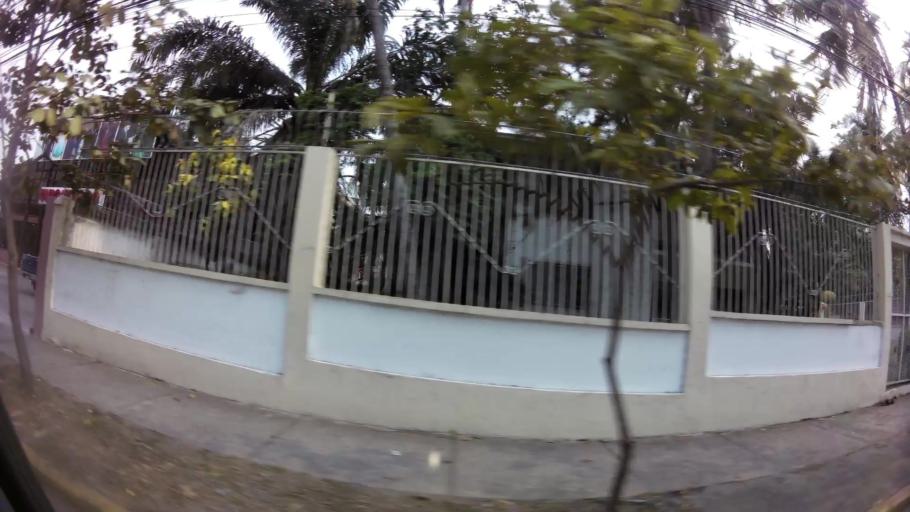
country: HN
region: Cortes
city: San Pedro Sula
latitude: 15.5064
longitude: -88.0337
